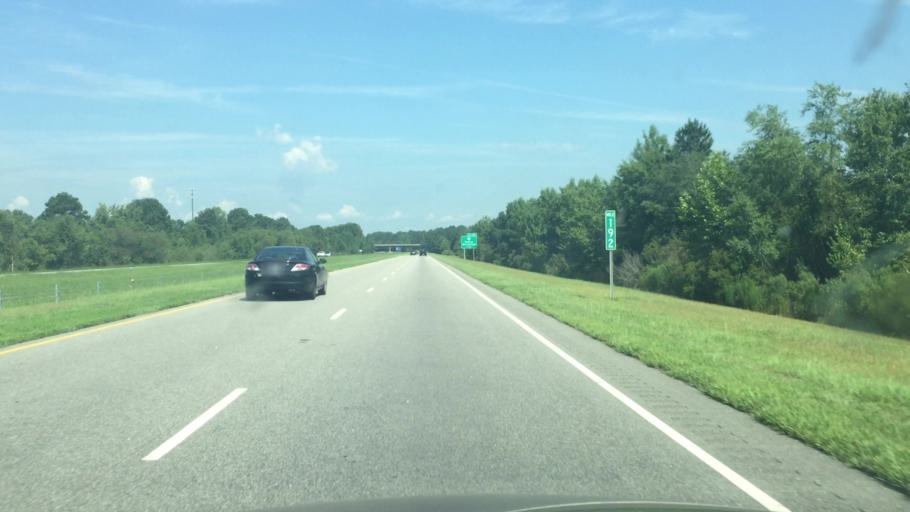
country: US
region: North Carolina
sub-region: Robeson County
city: Maxton
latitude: 34.7392
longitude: -79.3284
